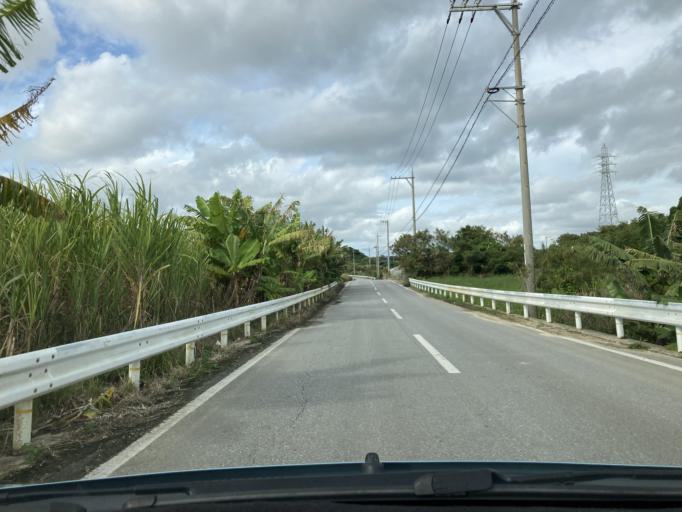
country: JP
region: Okinawa
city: Itoman
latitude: 26.1163
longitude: 127.6878
